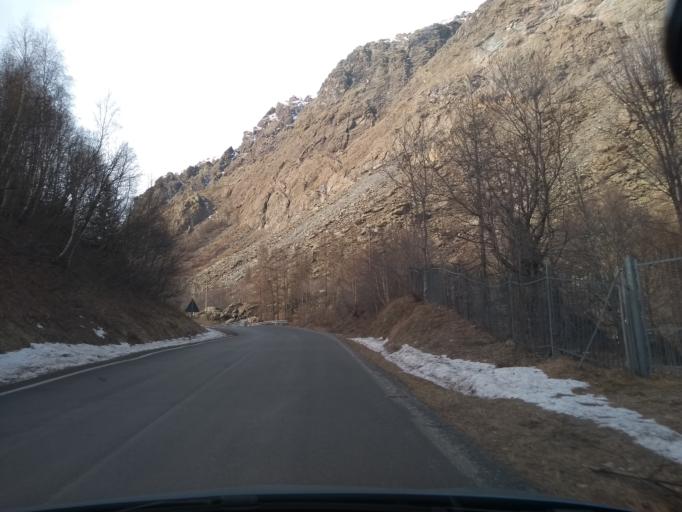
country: IT
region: Piedmont
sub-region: Provincia di Torino
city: Balme
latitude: 45.3033
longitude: 7.2291
